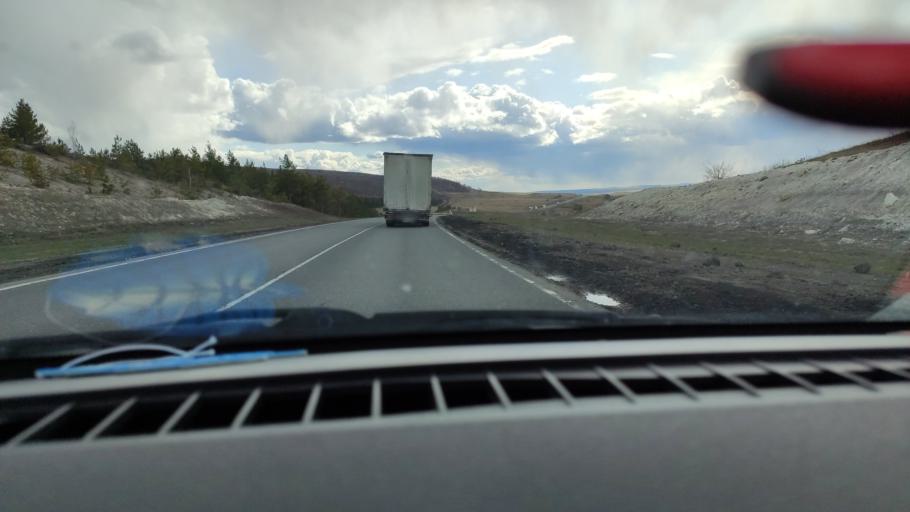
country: RU
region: Saratov
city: Alekseyevka
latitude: 52.3680
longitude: 47.9647
